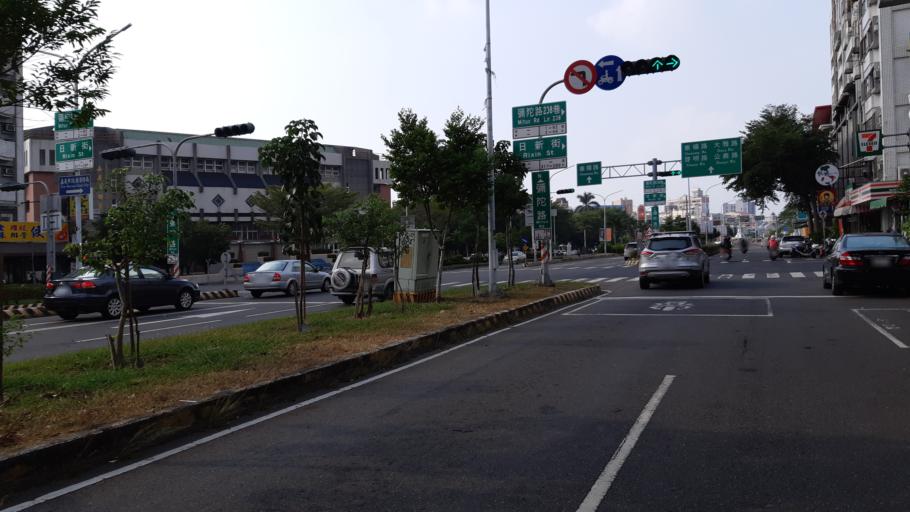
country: TW
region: Taiwan
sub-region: Chiayi
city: Jiayi Shi
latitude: 23.4731
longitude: 120.4634
